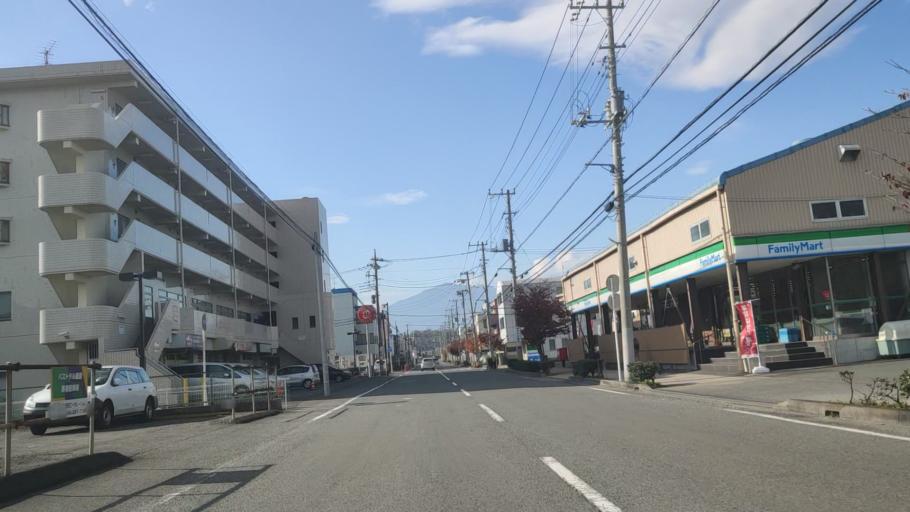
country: JP
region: Kanagawa
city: Atsugi
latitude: 35.4288
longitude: 139.3630
